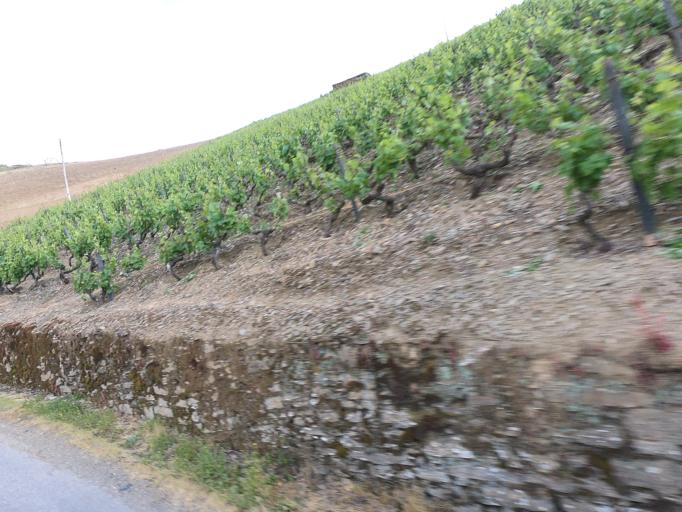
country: PT
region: Vila Real
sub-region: Vila Real
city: Vila Real
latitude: 41.2191
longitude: -7.7123
